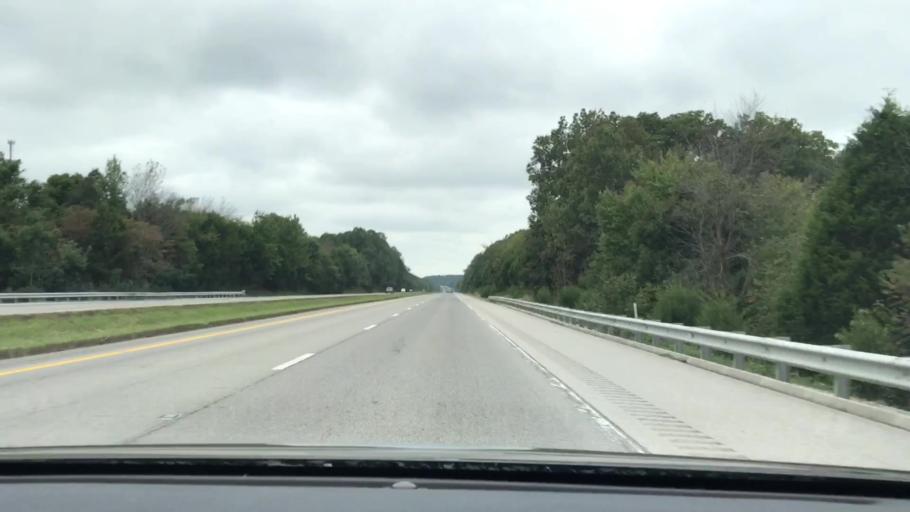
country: US
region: Kentucky
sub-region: Barren County
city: Glasgow
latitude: 36.9955
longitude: -85.7656
